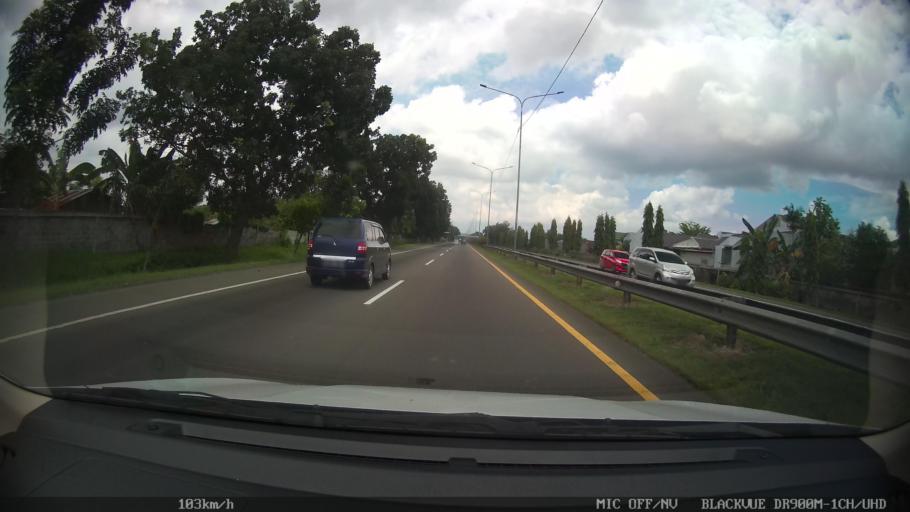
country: ID
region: North Sumatra
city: Medan
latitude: 3.6168
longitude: 98.7209
